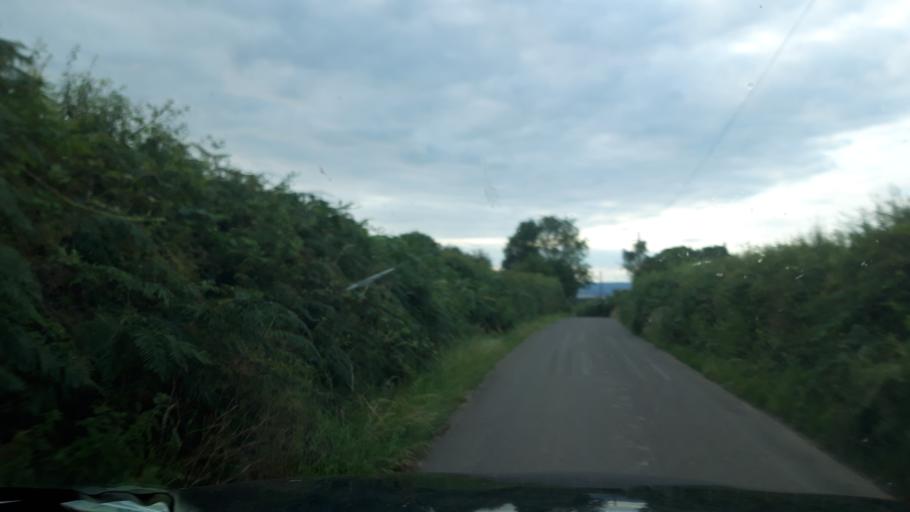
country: IE
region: Leinster
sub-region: Kilkenny
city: Graiguenamanagh
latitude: 52.5706
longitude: -6.9810
